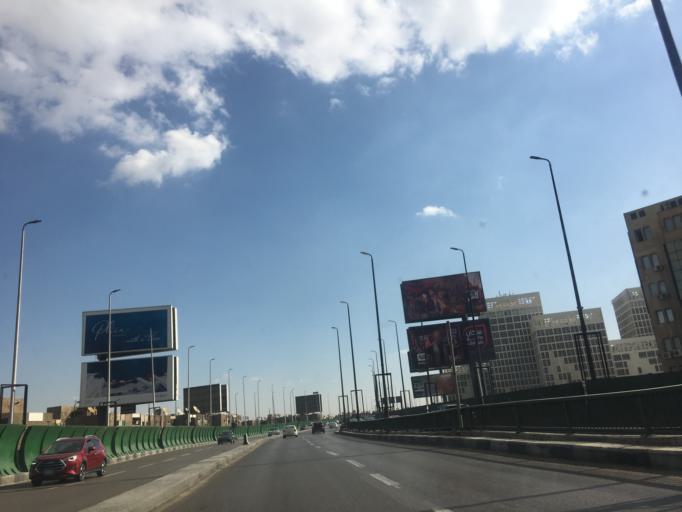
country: EG
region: Muhafazat al Qahirah
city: Cairo
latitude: 30.0627
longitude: 31.2995
